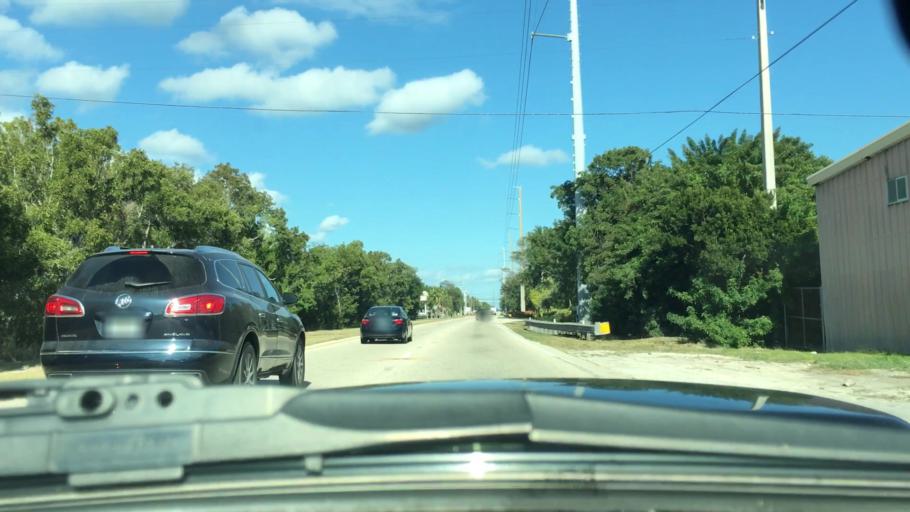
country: US
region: Florida
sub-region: Monroe County
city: Key Largo
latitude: 25.0724
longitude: -80.4644
